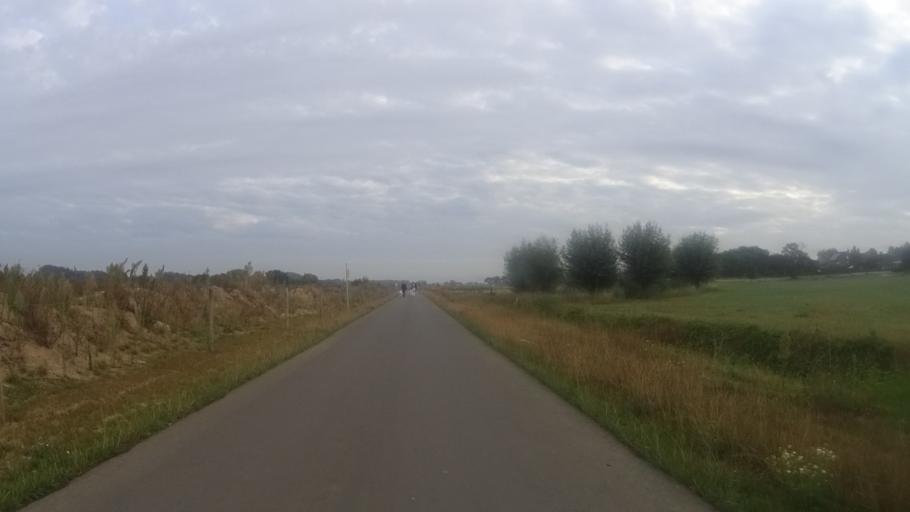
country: NL
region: Limburg
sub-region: Gemeente Venlo
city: Arcen
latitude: 51.4447
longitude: 6.1632
